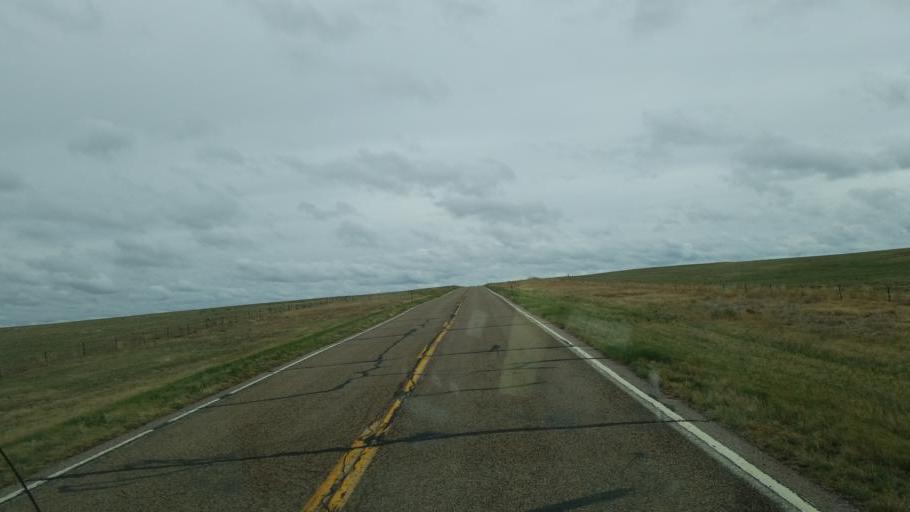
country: US
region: Colorado
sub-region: Lincoln County
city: Hugo
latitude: 38.8503
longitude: -103.4418
